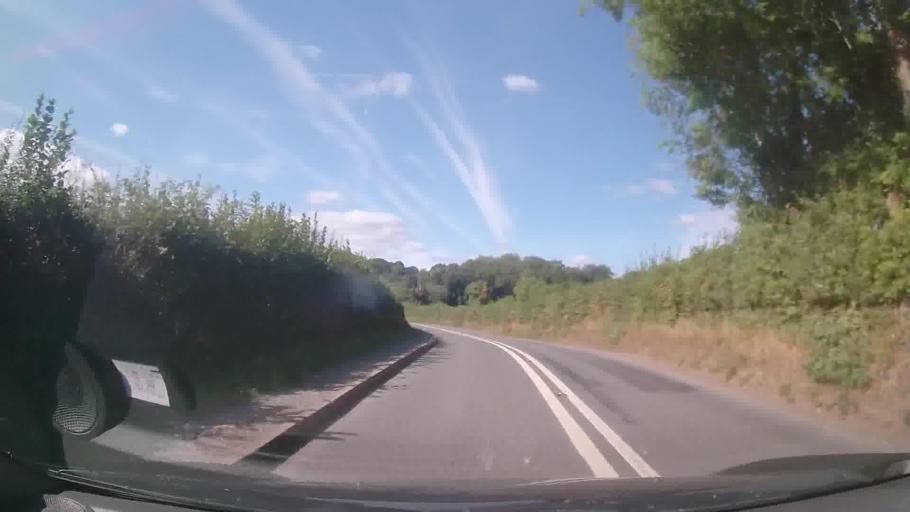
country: GB
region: Wales
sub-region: Sir Powys
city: Hay
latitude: 52.0831
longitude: -3.1424
